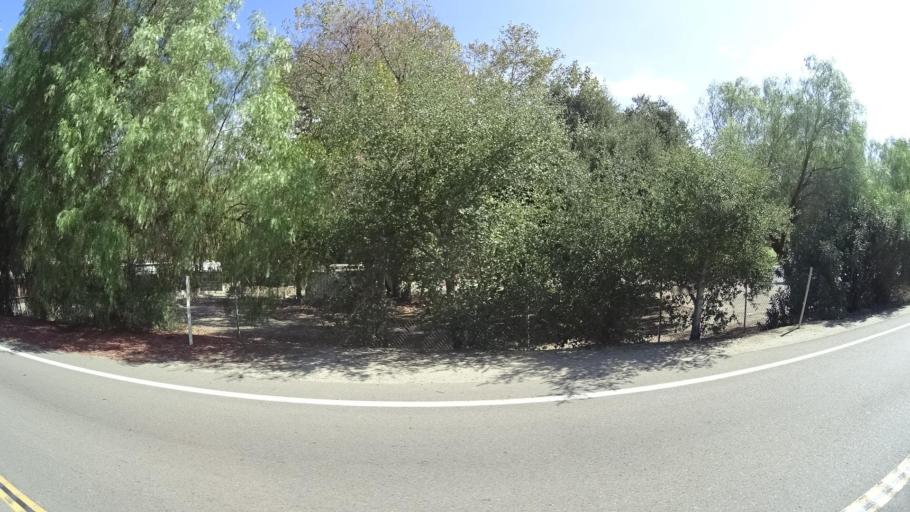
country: US
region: California
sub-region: San Diego County
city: Crest
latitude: 32.7992
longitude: -116.8452
